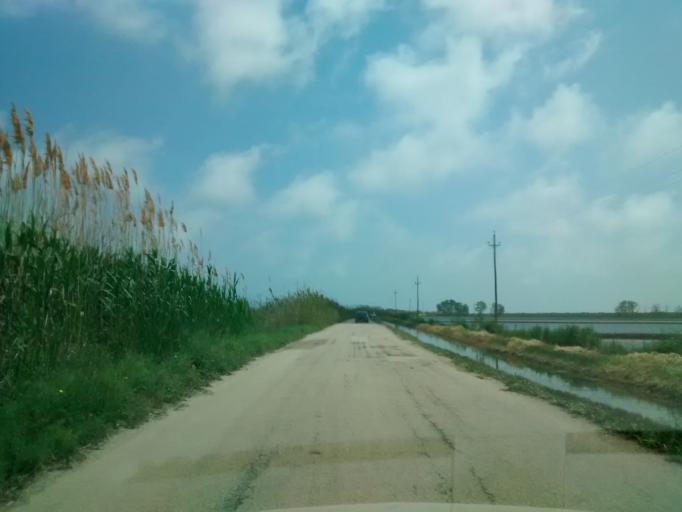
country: ES
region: Catalonia
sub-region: Provincia de Tarragona
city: Deltebre
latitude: 40.6979
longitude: 0.8335
